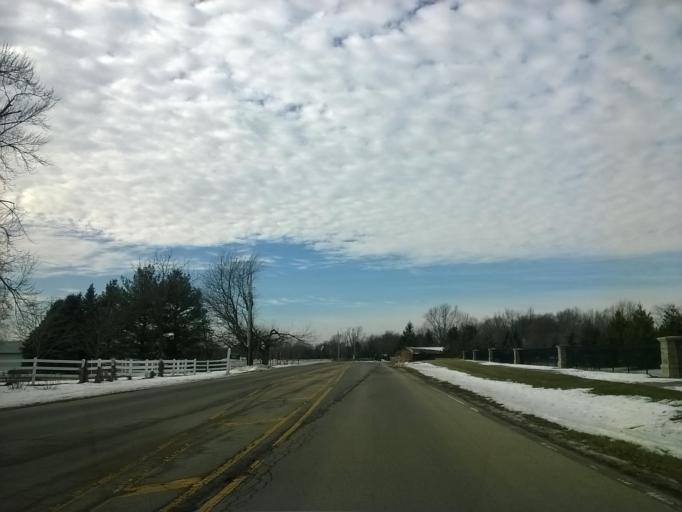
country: US
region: Indiana
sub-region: Boone County
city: Zionsville
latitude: 39.9772
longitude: -86.2385
